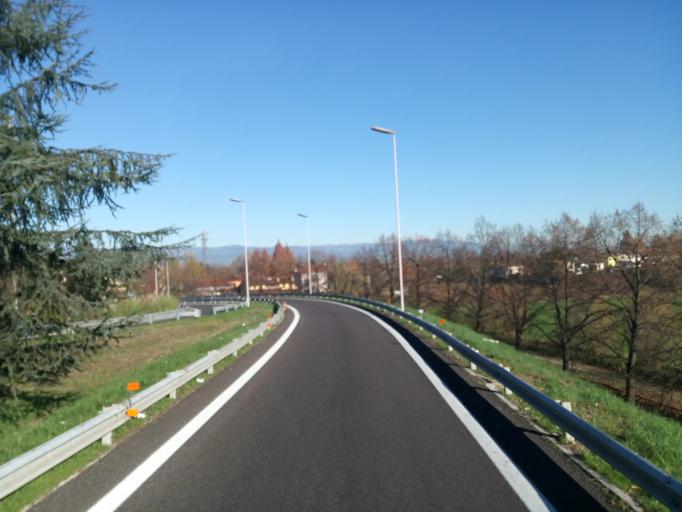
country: IT
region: Veneto
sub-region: Provincia di Vicenza
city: Lisiera
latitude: 45.5780
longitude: 11.6032
